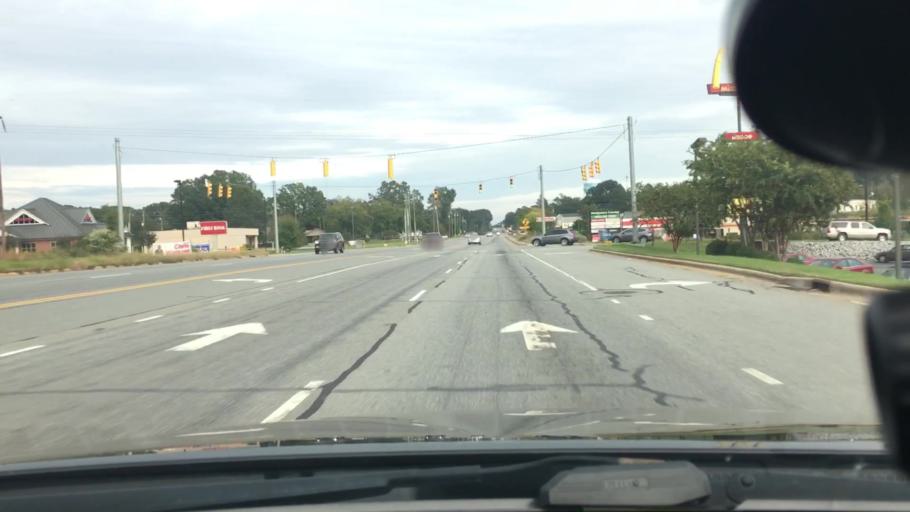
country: US
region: North Carolina
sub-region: Montgomery County
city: Biscoe
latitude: 35.3589
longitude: -79.7982
